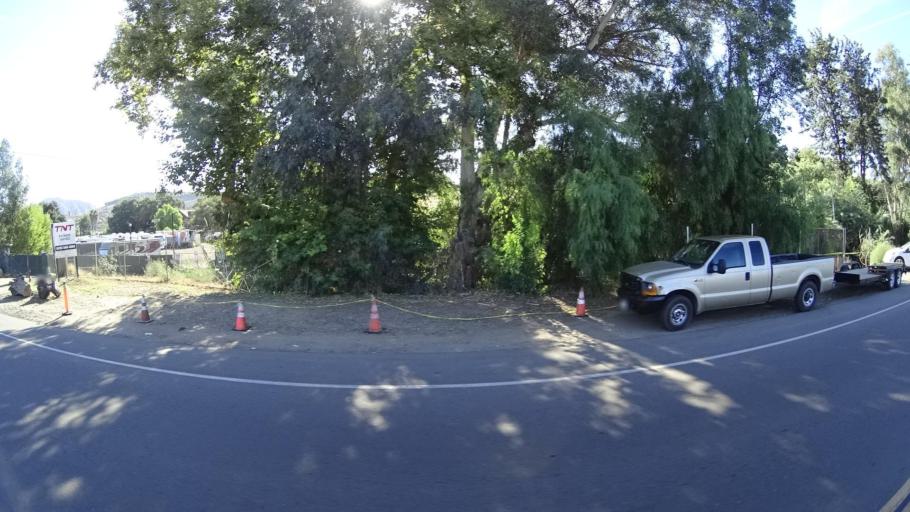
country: US
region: California
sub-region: San Diego County
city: Lakeside
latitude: 32.8379
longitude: -116.8972
